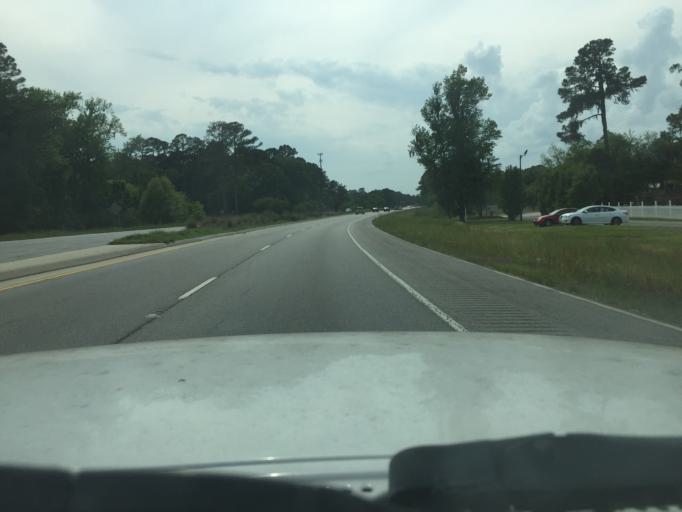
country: US
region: Georgia
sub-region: Chatham County
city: Wilmington Island
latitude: 32.0317
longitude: -80.9654
